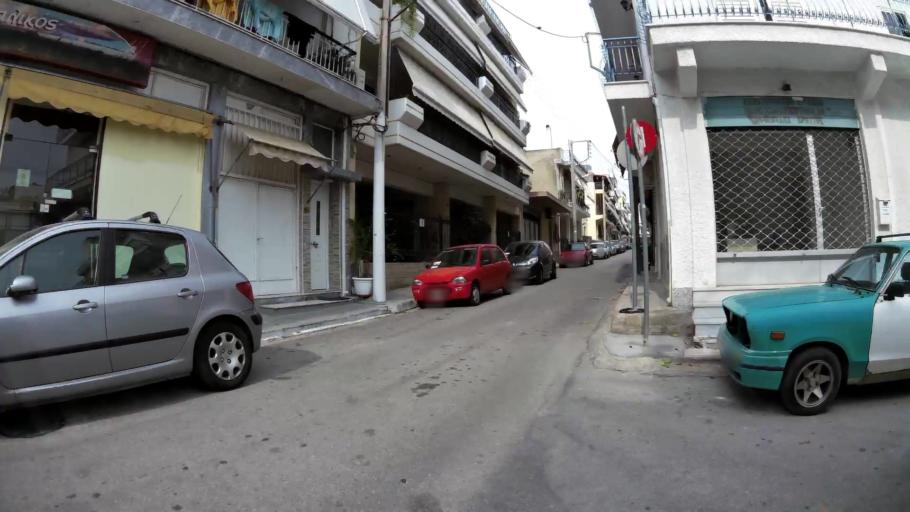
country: GR
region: Attica
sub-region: Nomarchia Athinas
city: Peristeri
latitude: 38.0128
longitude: 23.6805
